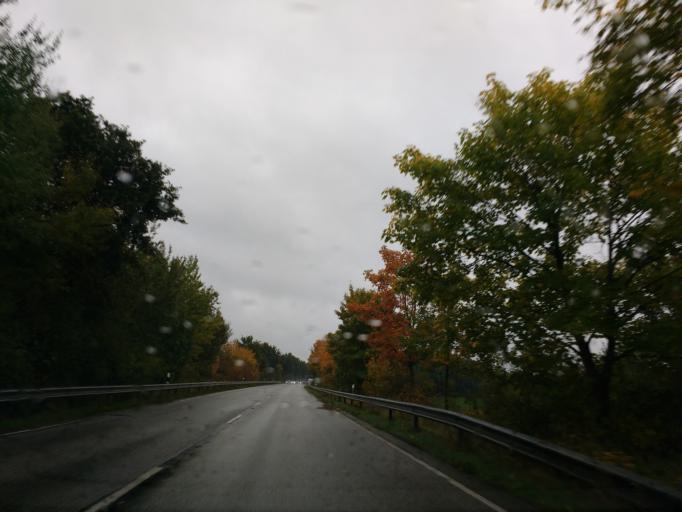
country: DE
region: Schleswig-Holstein
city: Susel
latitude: 54.0755
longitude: 10.7048
